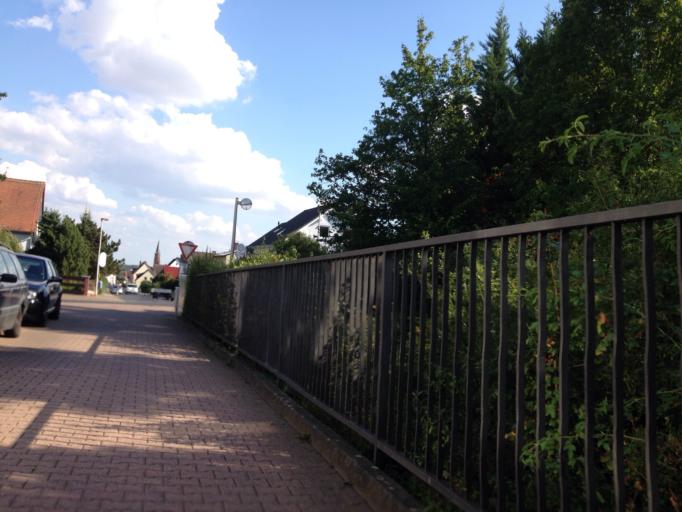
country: DE
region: Hesse
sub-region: Regierungsbezirk Darmstadt
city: Friedrichsdorf
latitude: 50.2472
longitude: 8.6445
